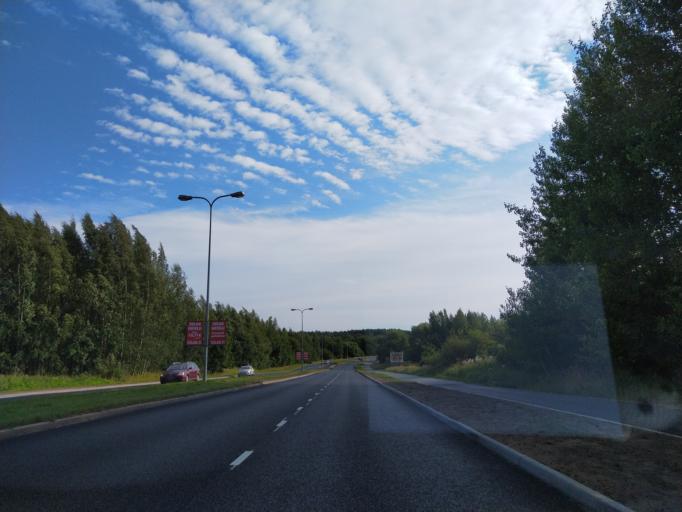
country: FI
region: Varsinais-Suomi
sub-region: Turku
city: Turku
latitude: 60.4268
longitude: 22.2397
